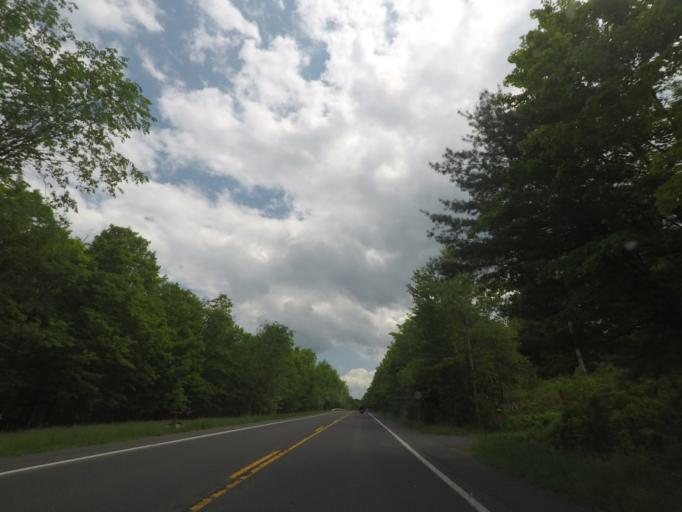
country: US
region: New York
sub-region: Dutchess County
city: Pine Plains
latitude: 42.1030
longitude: -73.6912
